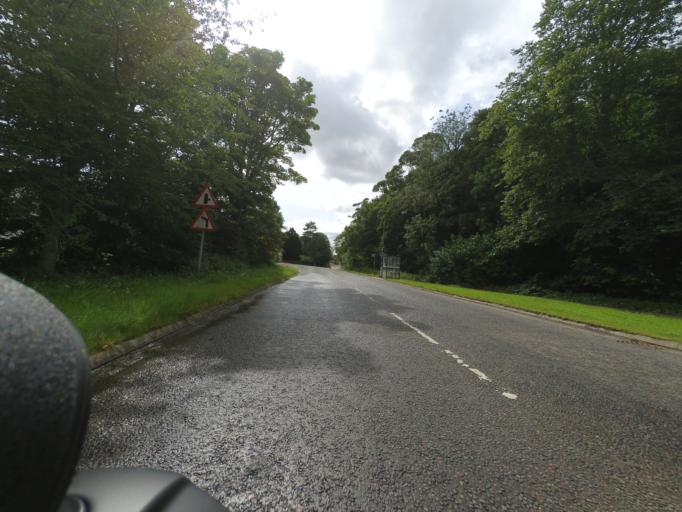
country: GB
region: Scotland
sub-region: Highland
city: Tain
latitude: 57.7475
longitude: -4.0723
